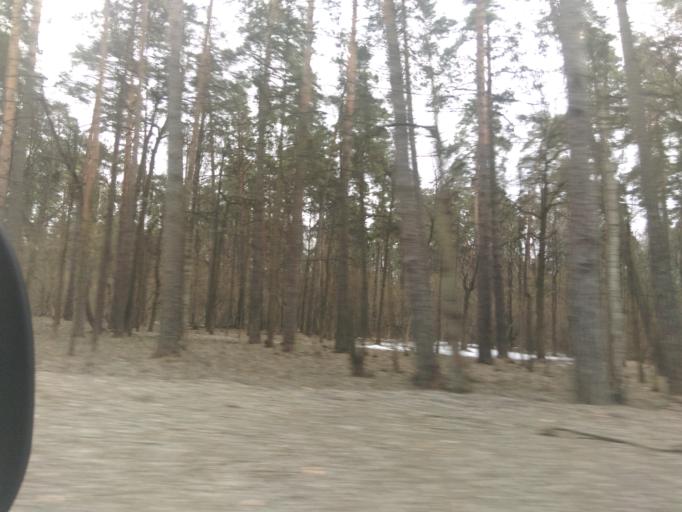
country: RU
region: Moscow
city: Rublevo
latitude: 55.7622
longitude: 37.3561
